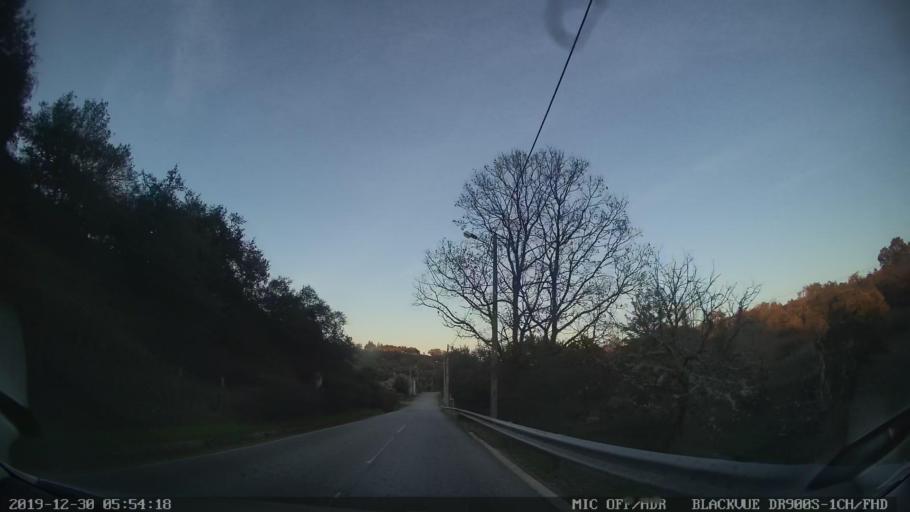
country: PT
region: Castelo Branco
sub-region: Idanha-A-Nova
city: Idanha-a-Nova
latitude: 40.0197
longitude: -7.2460
